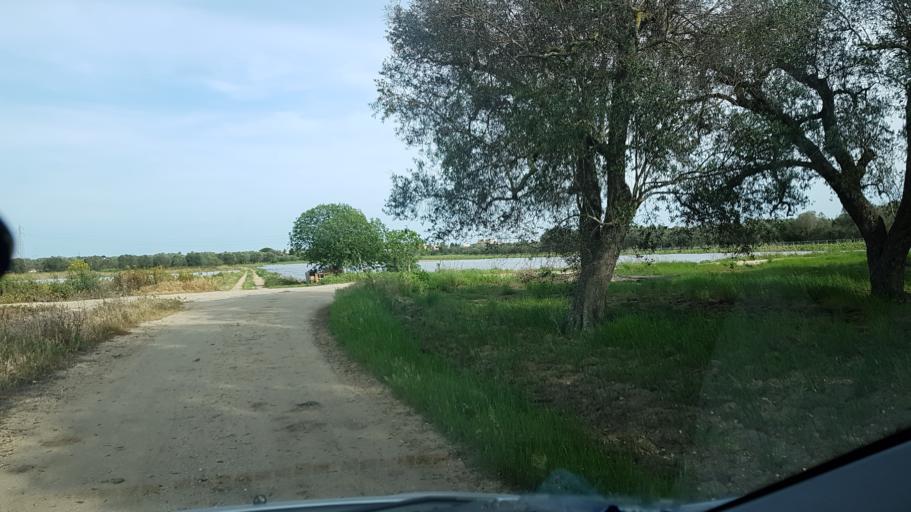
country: IT
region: Apulia
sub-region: Provincia di Brindisi
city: Tuturano
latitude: 40.5508
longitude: 17.9346
